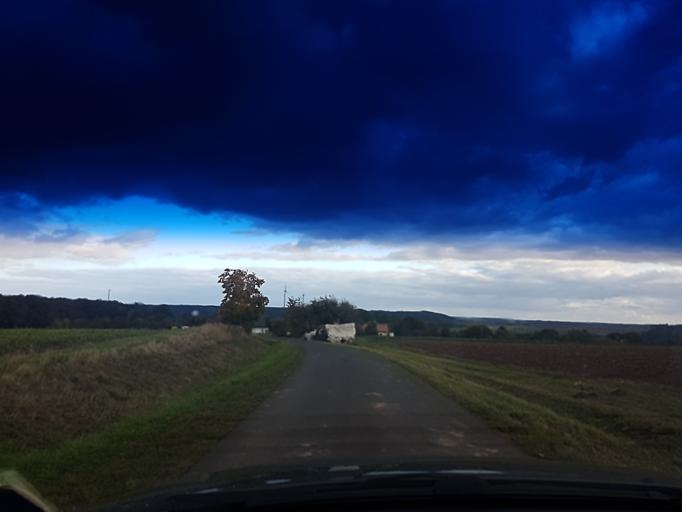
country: DE
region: Bavaria
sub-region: Regierungsbezirk Mittelfranken
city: Burghaslach
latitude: 49.7416
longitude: 10.5933
